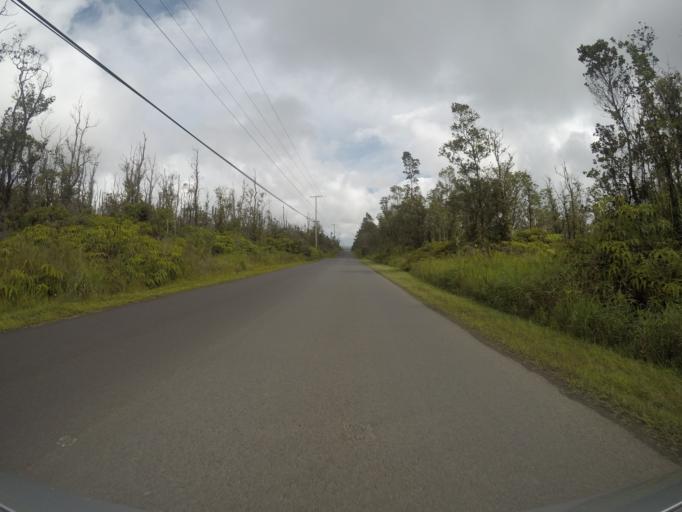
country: US
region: Hawaii
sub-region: Hawaii County
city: Fern Acres
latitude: 19.4686
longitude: -155.1361
